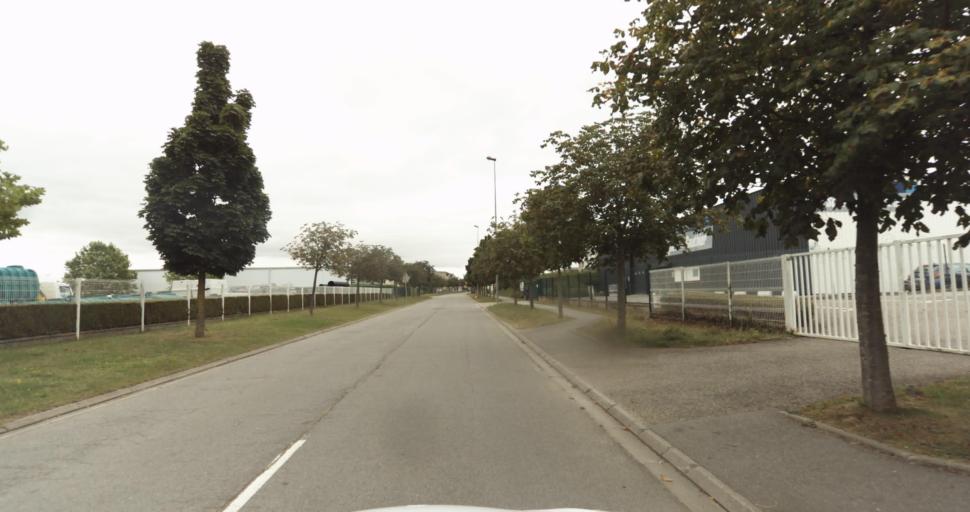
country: FR
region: Haute-Normandie
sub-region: Departement de l'Eure
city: Gravigny
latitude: 49.0334
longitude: 1.1831
